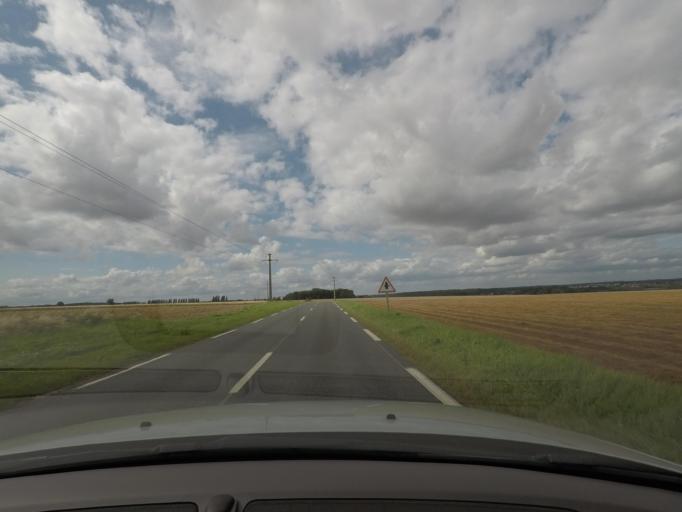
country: FR
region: Haute-Normandie
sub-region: Departement de l'Eure
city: Les Andelys
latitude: 49.2315
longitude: 1.4343
